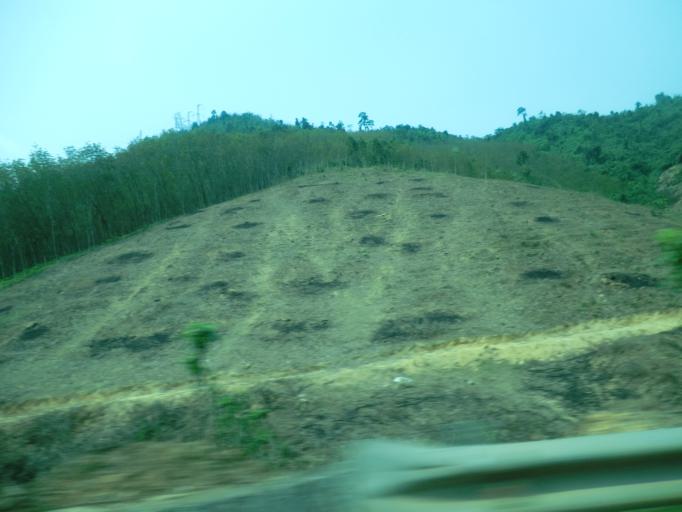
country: VN
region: Thanh Hoa
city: Thi Tran Yen Cat
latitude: 19.6164
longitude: 105.4031
